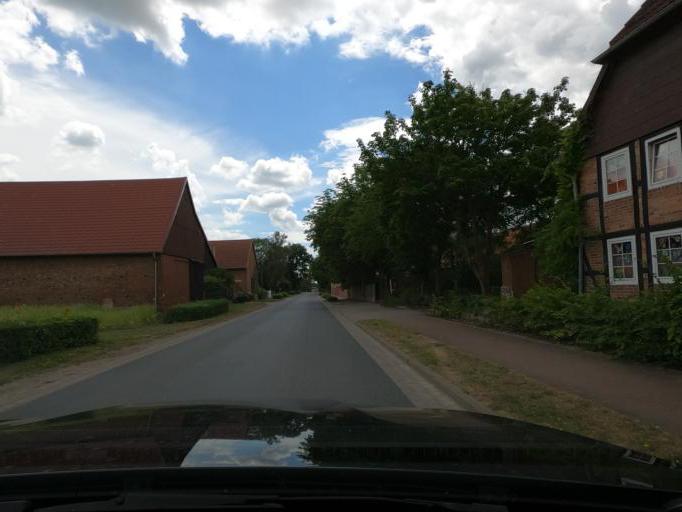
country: DE
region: Lower Saxony
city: Sehnde
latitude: 52.2849
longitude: 10.0143
